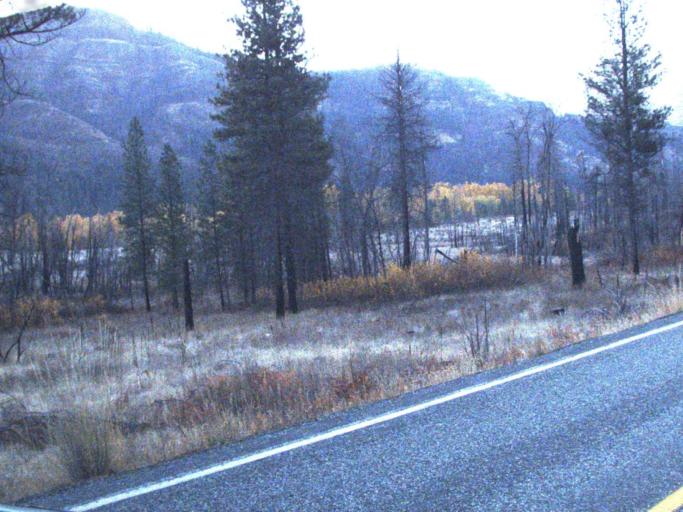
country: US
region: Washington
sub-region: Ferry County
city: Republic
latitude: 48.2502
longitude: -118.6925
